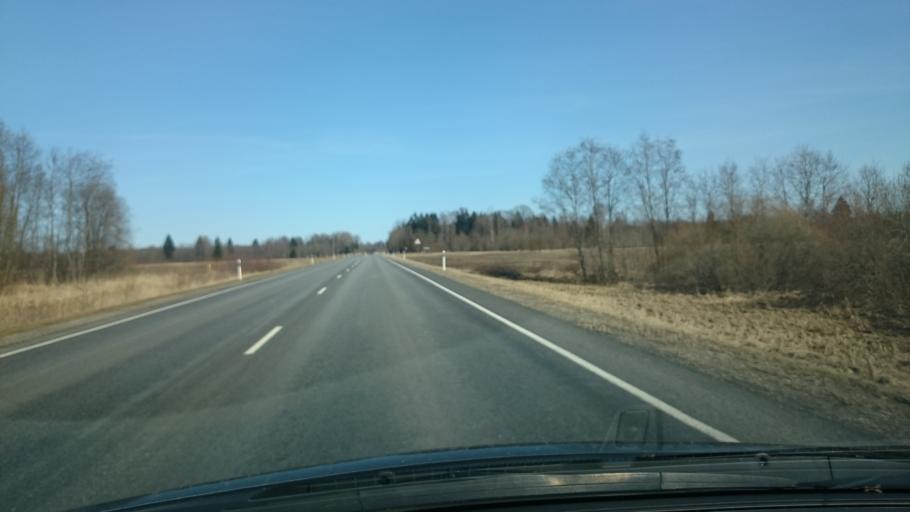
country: EE
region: Paernumaa
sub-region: Vaendra vald (alev)
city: Vandra
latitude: 58.6344
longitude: 24.9560
